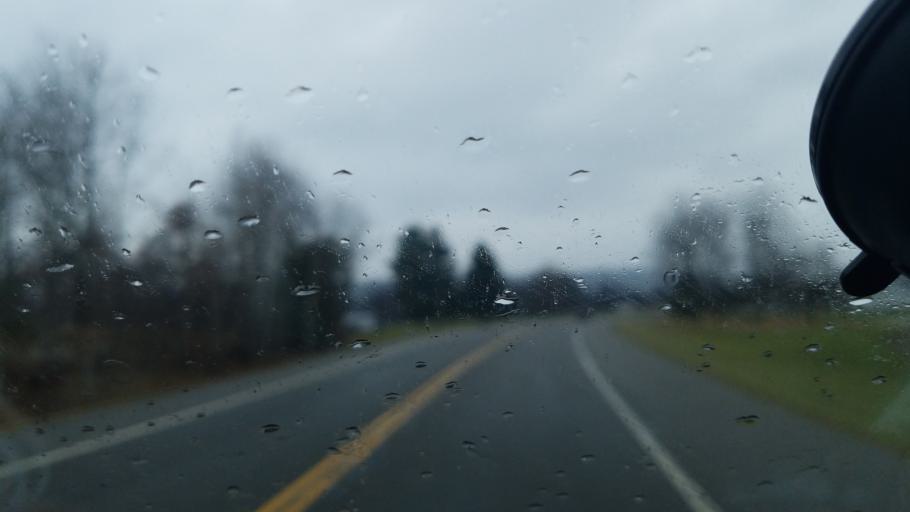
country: US
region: New York
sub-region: Allegany County
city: Wellsville
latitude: 42.0381
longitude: -77.9124
